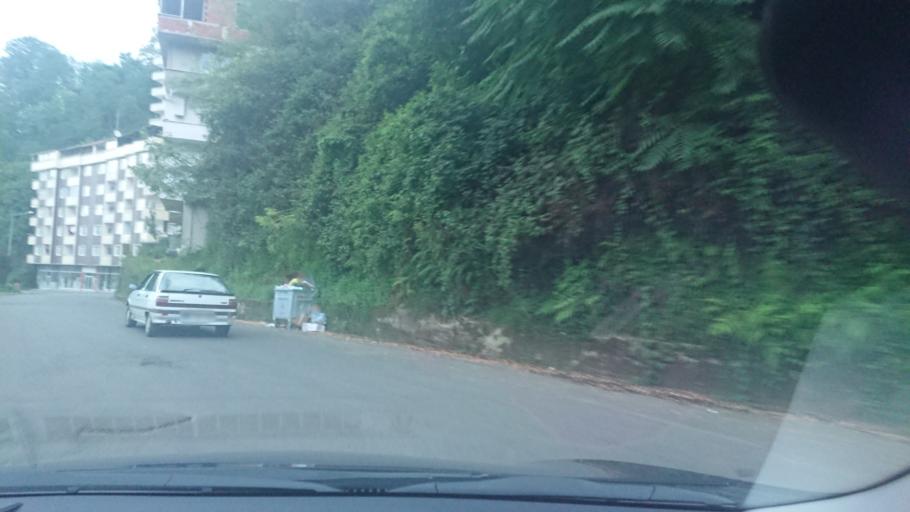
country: TR
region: Rize
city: Rize
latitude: 41.0242
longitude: 40.5111
